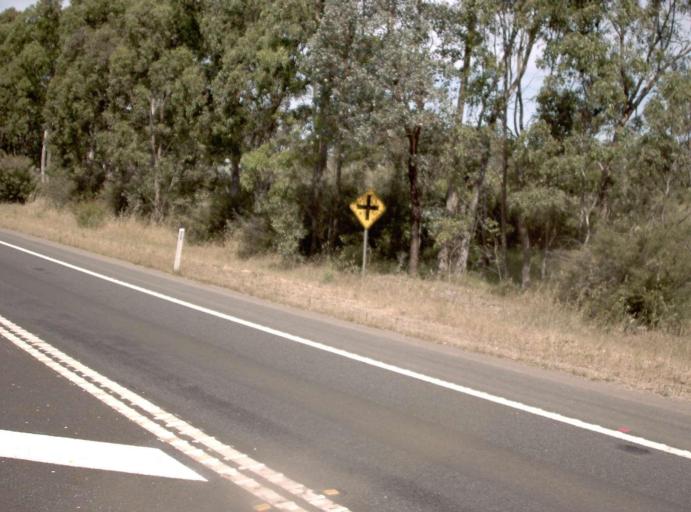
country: AU
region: Victoria
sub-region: Wellington
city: Sale
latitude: -37.9332
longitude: 147.1815
